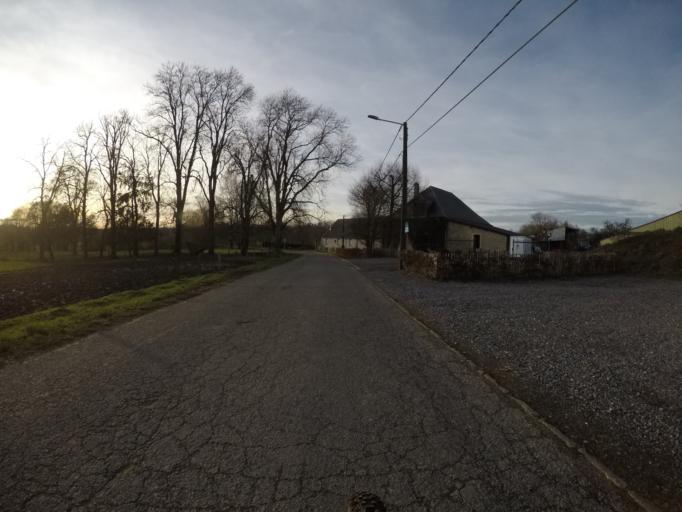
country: BE
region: Wallonia
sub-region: Province du Luxembourg
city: Tintigny
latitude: 49.6684
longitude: 5.4524
